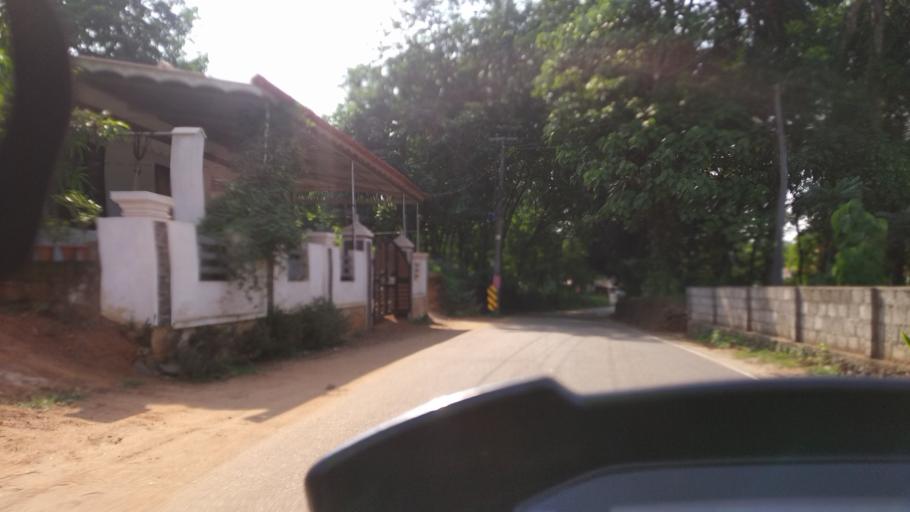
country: IN
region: Kerala
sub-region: Ernakulam
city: Piravam
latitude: 9.8539
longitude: 76.5280
